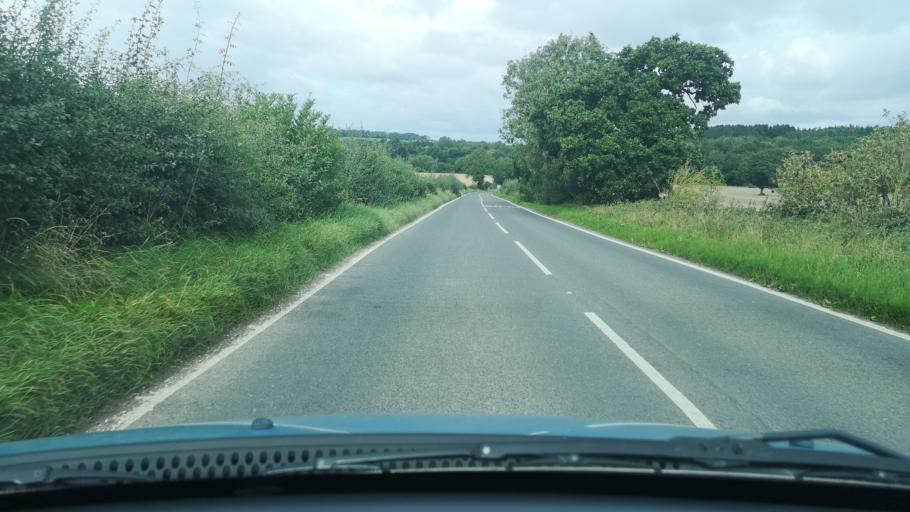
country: GB
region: England
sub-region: Barnsley
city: Royston
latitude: 53.6233
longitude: -1.4490
